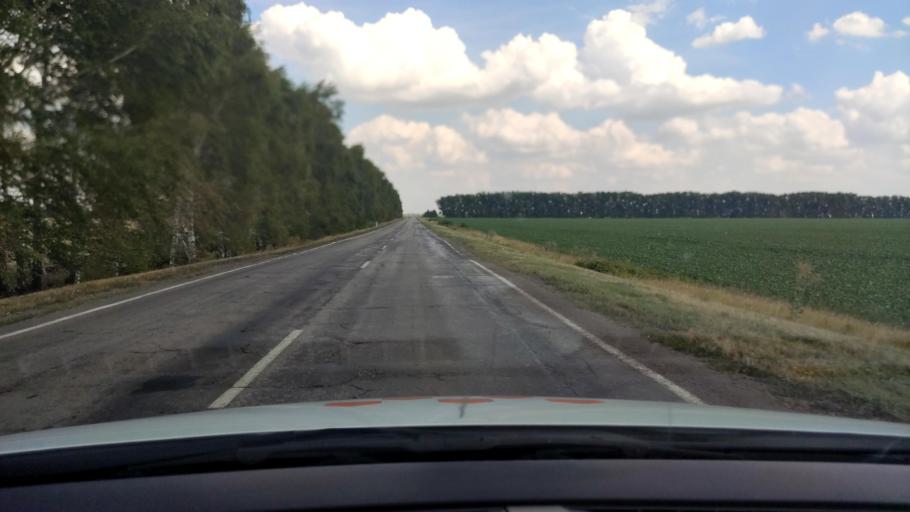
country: RU
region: Voronezj
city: Ertil'
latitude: 51.7880
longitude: 40.6184
